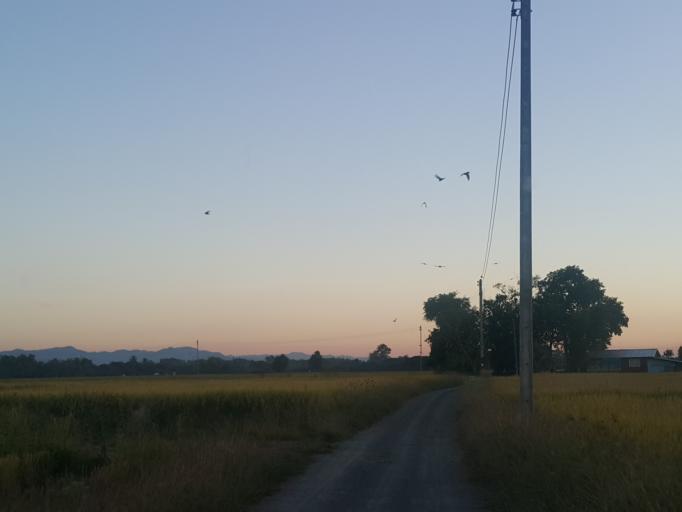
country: TH
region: Chiang Mai
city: San Kamphaeng
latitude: 18.8282
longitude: 99.1533
